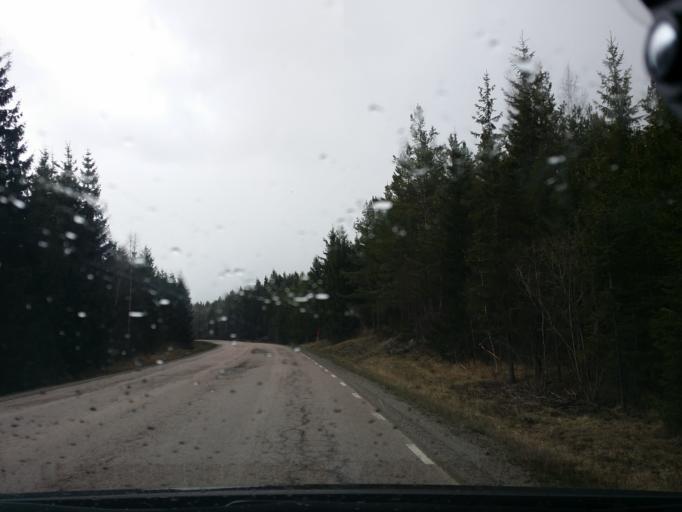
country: SE
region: Uppsala
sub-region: Enkopings Kommun
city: Enkoping
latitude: 59.6314
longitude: 17.1441
